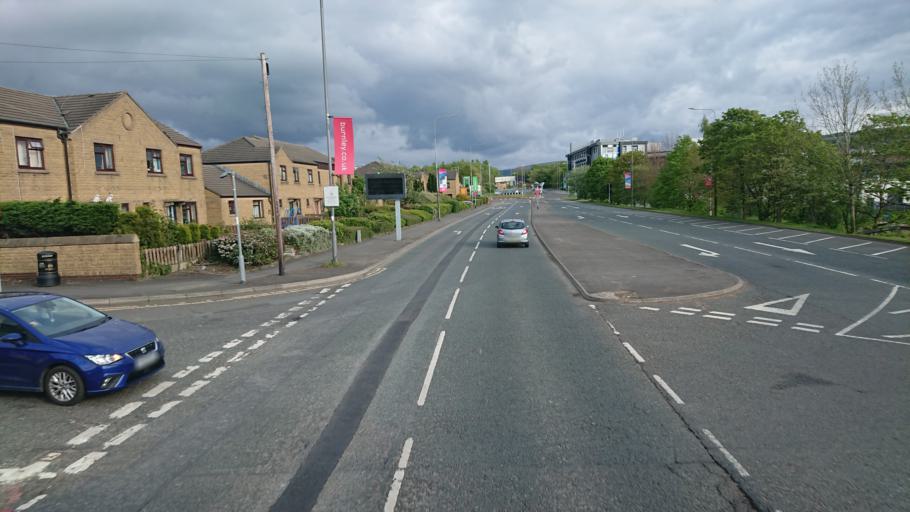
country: GB
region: England
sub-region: Lancashire
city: Burnley
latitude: 53.7960
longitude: -2.2492
